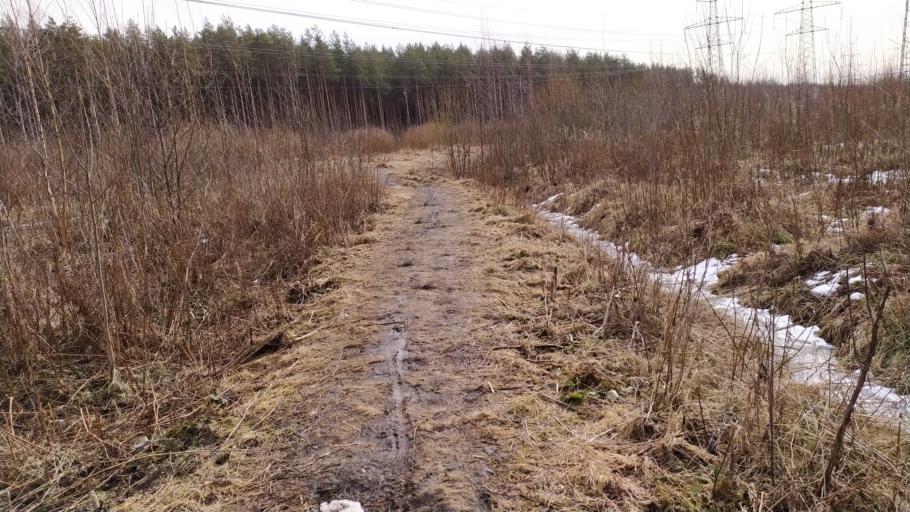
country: RU
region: St.-Petersburg
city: Krasnogvargeisky
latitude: 59.9604
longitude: 30.5008
